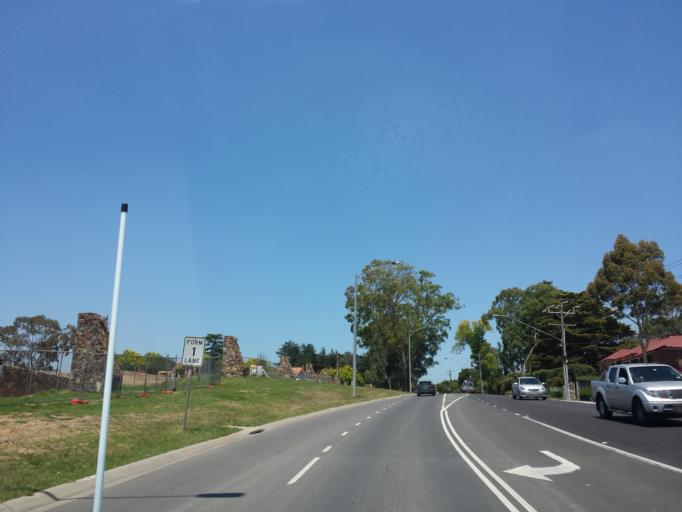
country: AU
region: Victoria
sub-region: Maroondah
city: Croydon North
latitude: -37.7796
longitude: 145.2938
